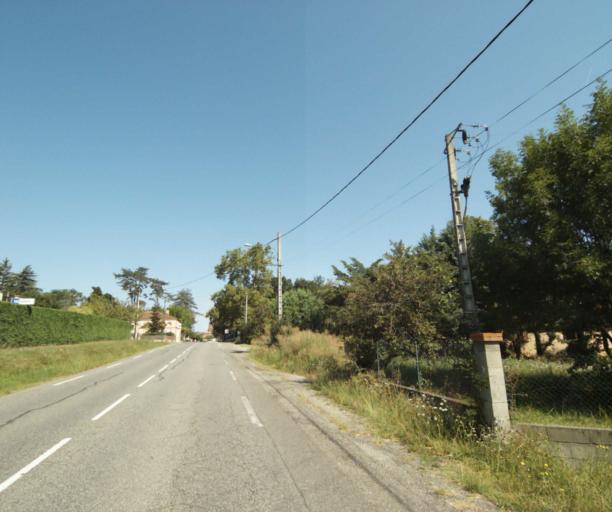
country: FR
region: Midi-Pyrenees
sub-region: Departement de l'Ariege
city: Lezat-sur-Leze
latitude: 43.2702
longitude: 1.3496
